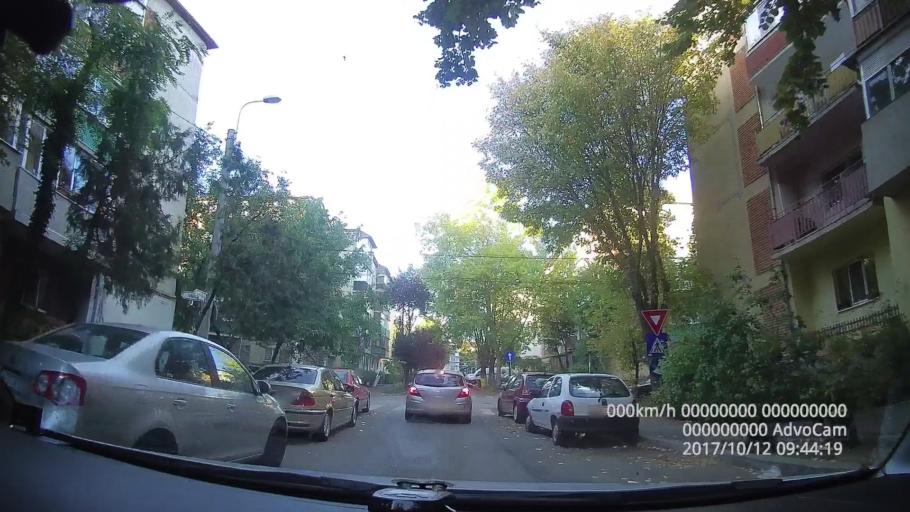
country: RO
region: Timis
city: Timisoara
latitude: 45.7735
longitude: 21.2301
